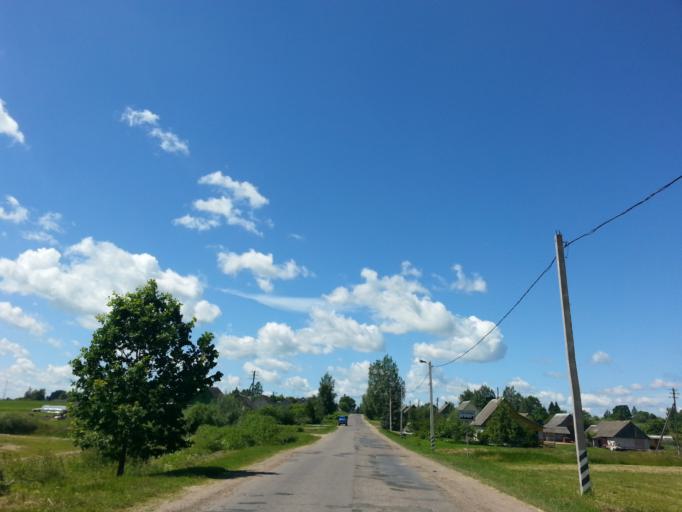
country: BY
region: Vitebsk
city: Mosar
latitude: 55.2098
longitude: 27.5519
